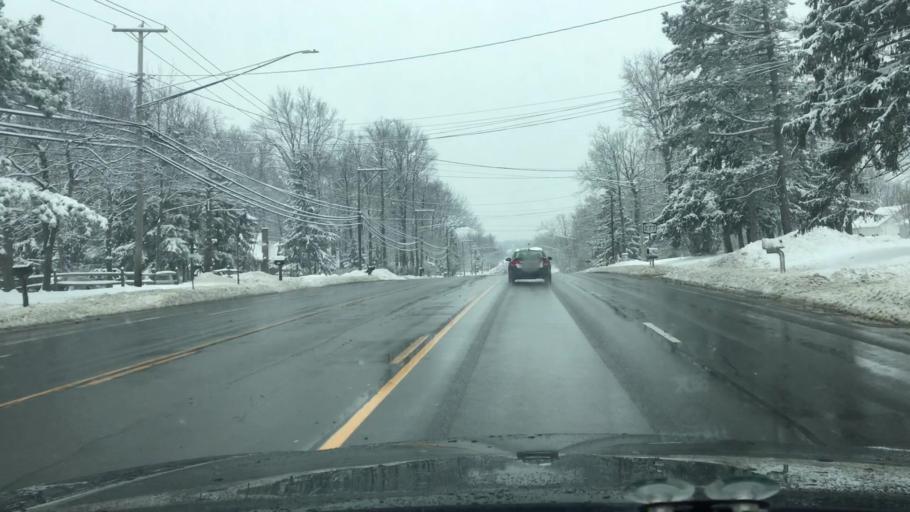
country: US
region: New York
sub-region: Erie County
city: Orchard Park
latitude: 42.8092
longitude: -78.7519
